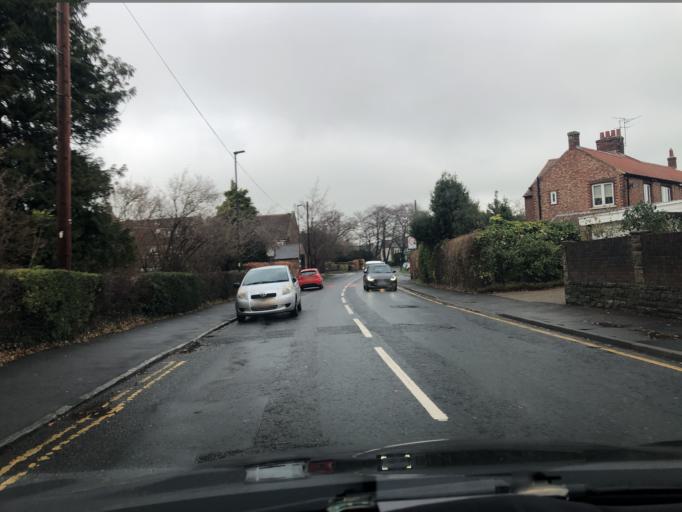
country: GB
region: England
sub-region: North Yorkshire
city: Stokesley
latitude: 54.4724
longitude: -1.1887
